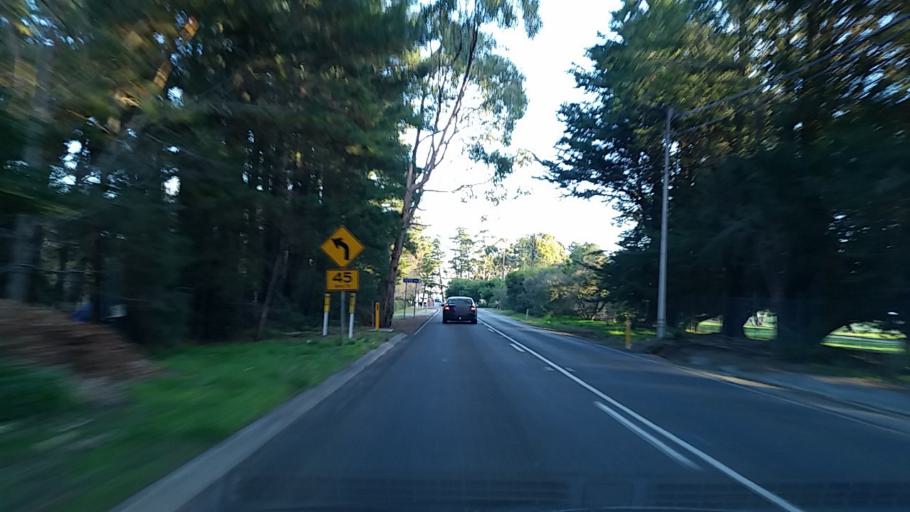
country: AU
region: South Australia
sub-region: Adelaide Hills
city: Upper Sturt
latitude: -35.0563
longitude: 138.6796
